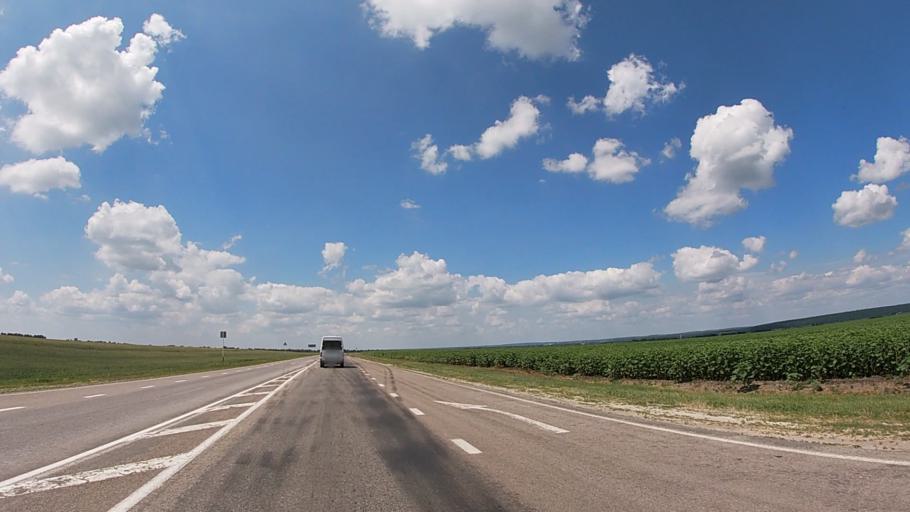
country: RU
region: Belgorod
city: Borisovka
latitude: 50.5769
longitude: 36.0272
